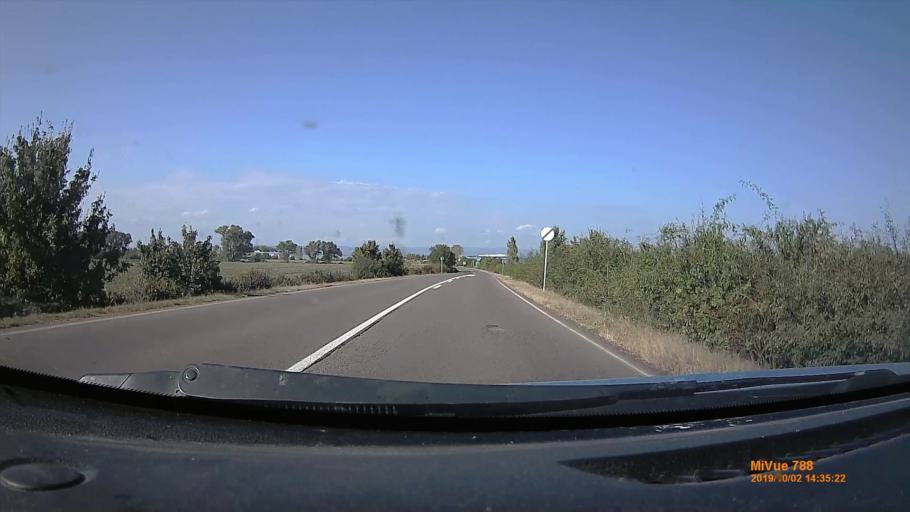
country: HU
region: Borsod-Abauj-Zemplen
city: Mezokovesd
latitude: 47.7829
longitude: 20.5807
